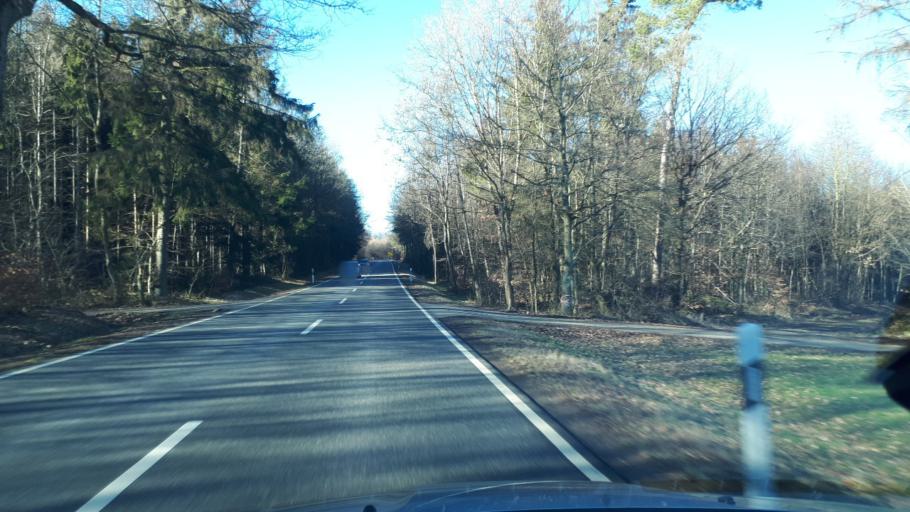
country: DE
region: Rheinland-Pfalz
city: Ellscheid
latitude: 50.1577
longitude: 6.9237
